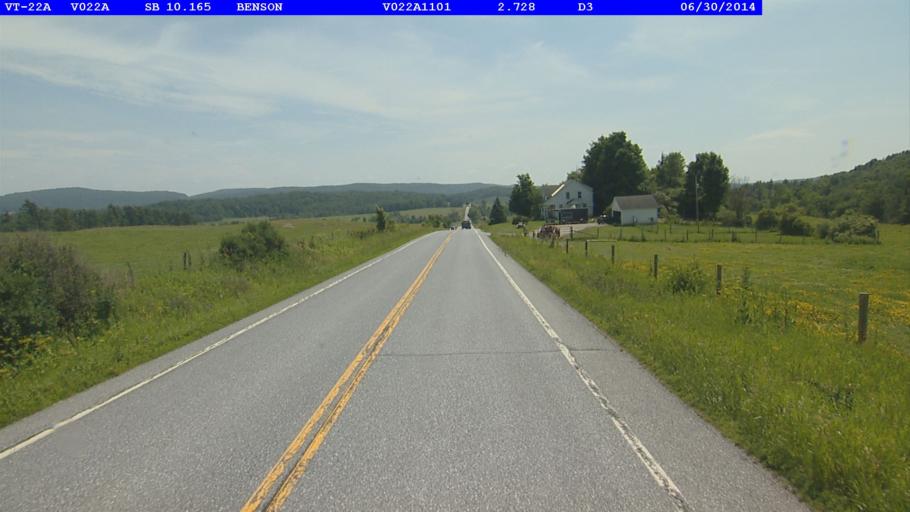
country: US
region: Vermont
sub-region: Rutland County
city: Fair Haven
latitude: 43.7077
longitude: -73.2969
